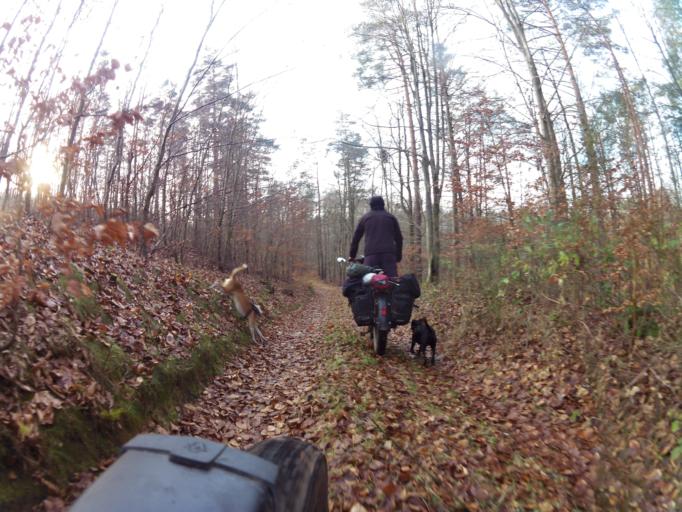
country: PL
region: West Pomeranian Voivodeship
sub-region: Powiat koszalinski
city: Polanow
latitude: 54.1896
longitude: 16.7296
